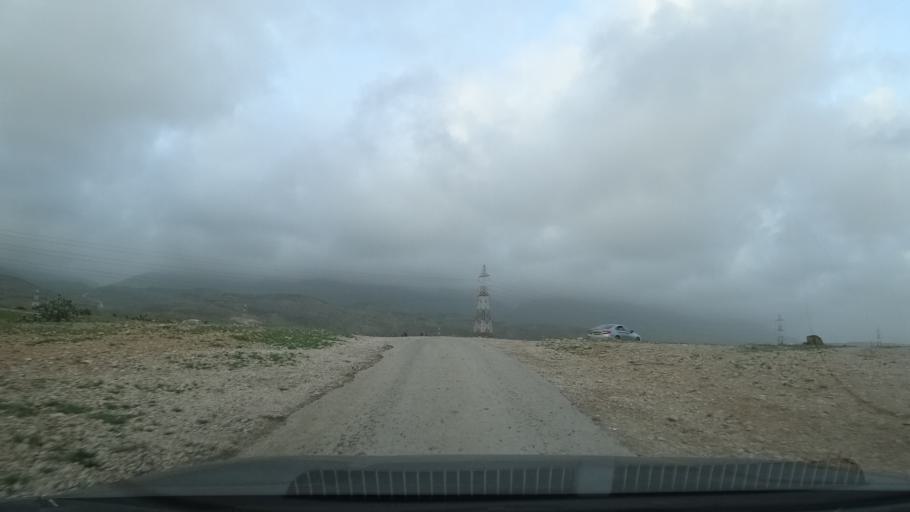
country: OM
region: Zufar
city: Salalah
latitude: 17.1018
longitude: 54.2337
